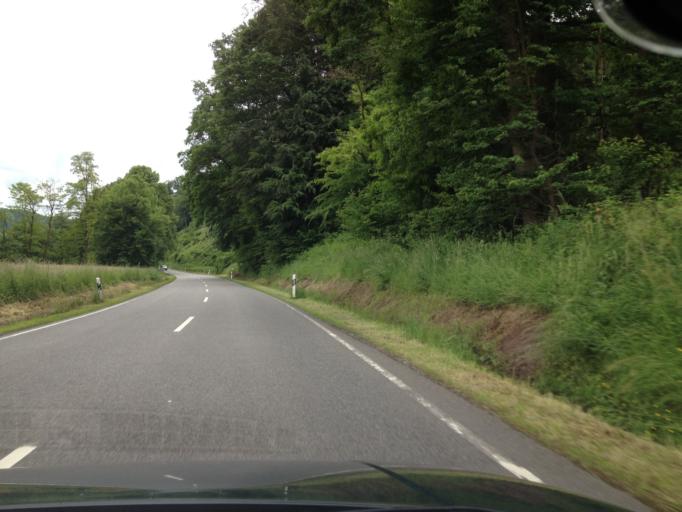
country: DE
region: Saarland
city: Homburg
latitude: 49.2937
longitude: 7.3005
